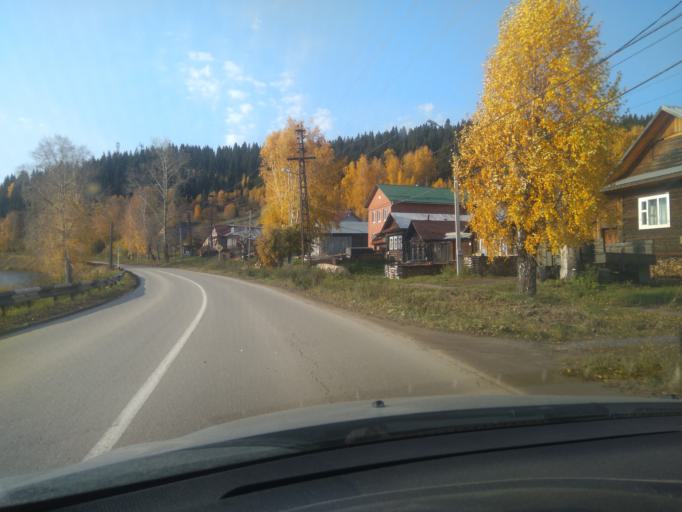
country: RU
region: Sverdlovsk
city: Nizhniye Sergi
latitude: 56.6750
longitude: 59.3215
